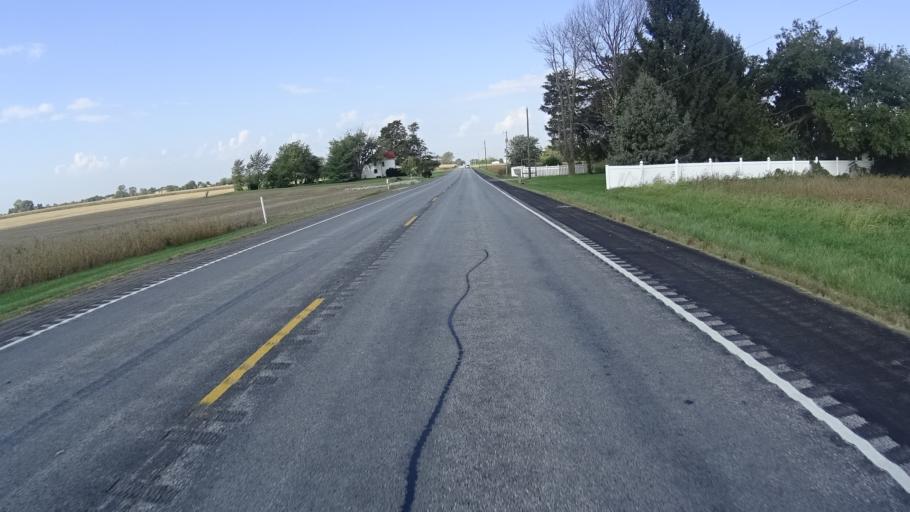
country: US
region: Indiana
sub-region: Madison County
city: Lapel
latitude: 40.0213
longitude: -85.8521
